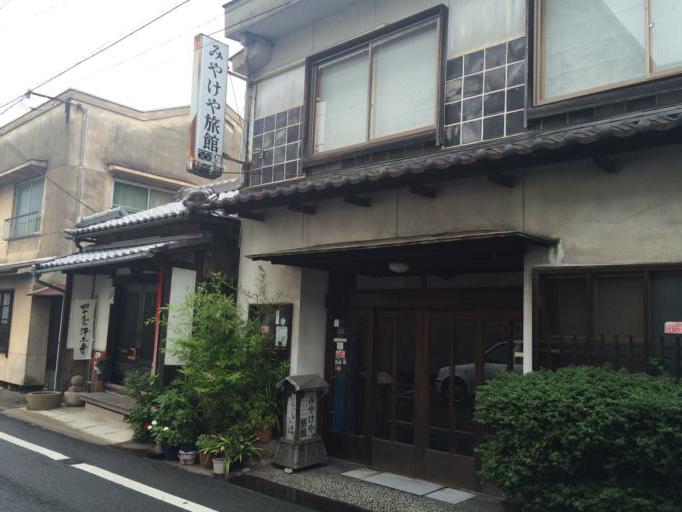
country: JP
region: Okayama
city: Kurashiki
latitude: 34.5987
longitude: 133.7644
